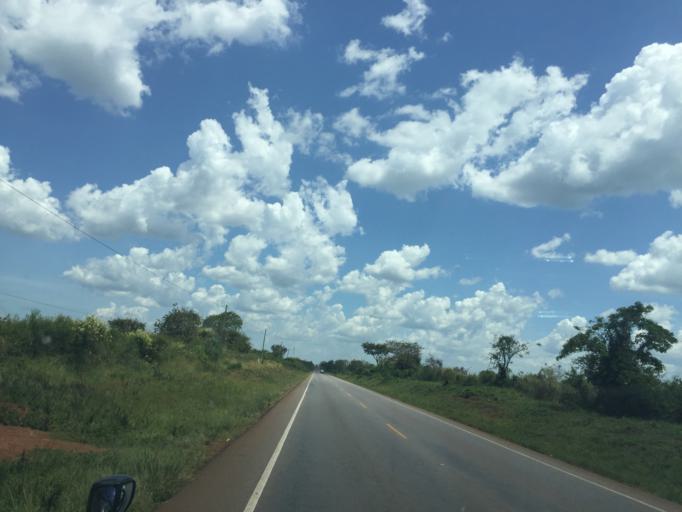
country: UG
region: Central Region
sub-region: Nakasongola District
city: Nakasongola
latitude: 1.3681
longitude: 32.3571
